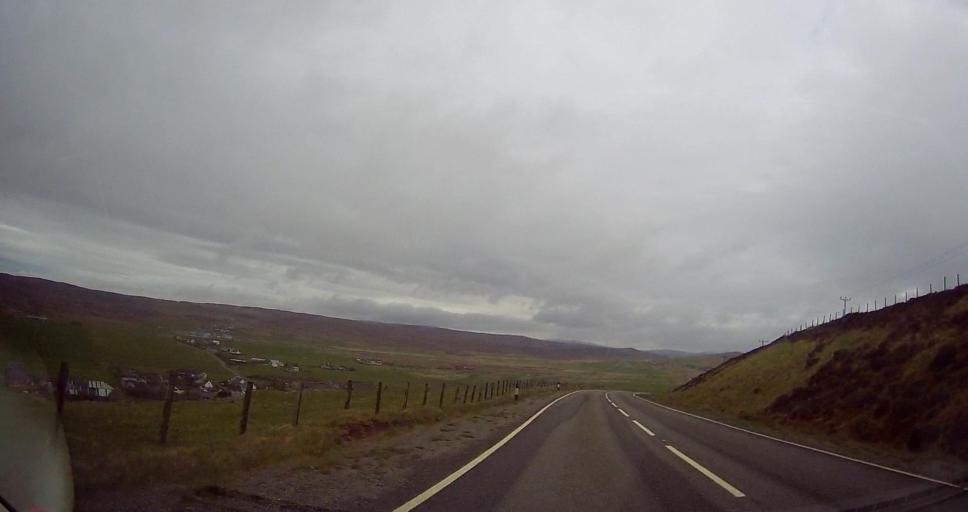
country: GB
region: Scotland
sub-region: Shetland Islands
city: Lerwick
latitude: 60.1789
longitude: -1.2243
